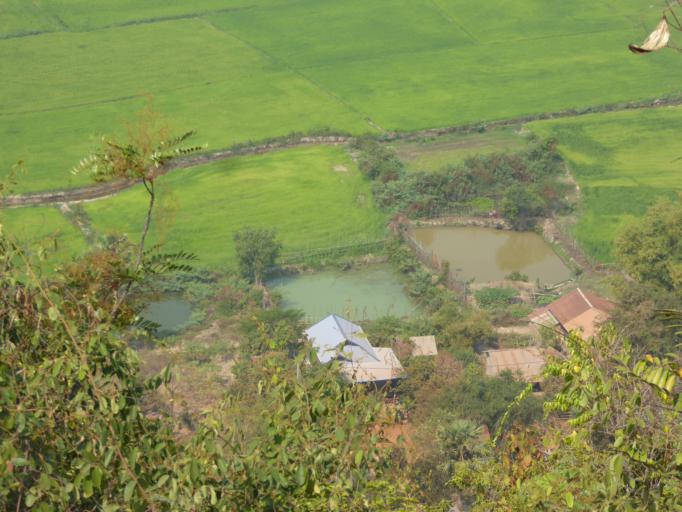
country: KH
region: Siem Reap
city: Siem Reap
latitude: 13.2854
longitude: 103.8113
